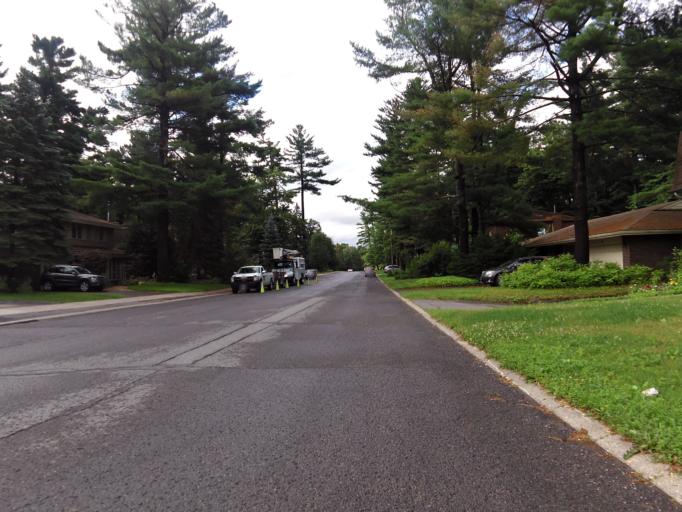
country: CA
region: Ontario
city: Bells Corners
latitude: 45.3250
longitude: -75.7871
